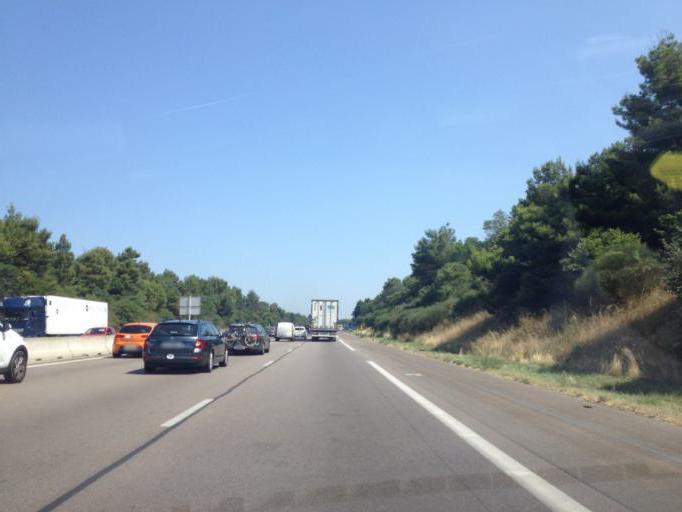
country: FR
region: Rhone-Alpes
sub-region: Departement de la Drome
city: Malataverne
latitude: 44.4927
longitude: 4.7674
